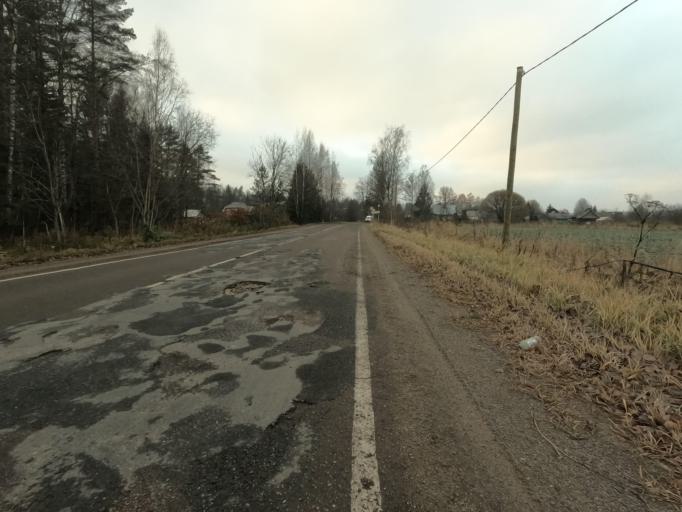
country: RU
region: Leningrad
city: Kirovsk
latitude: 59.8014
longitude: 30.9951
